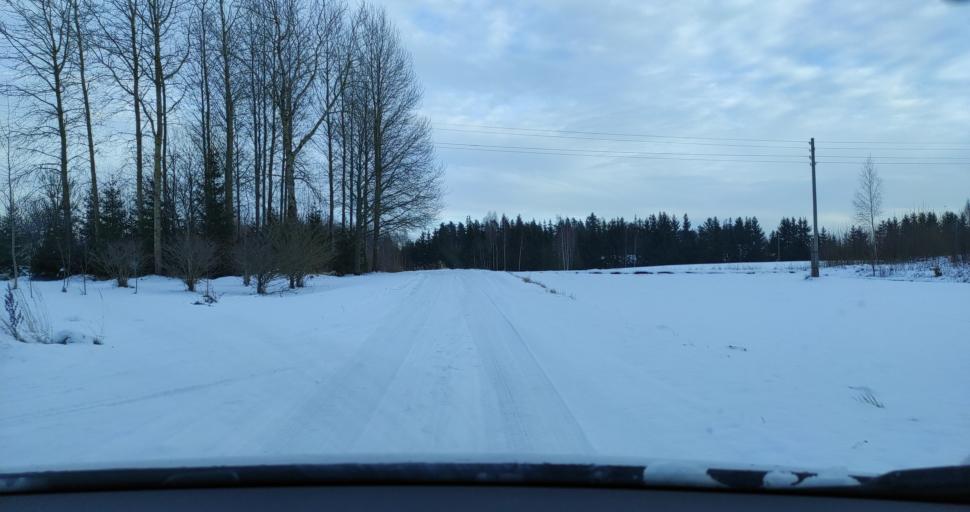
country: LV
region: Kuldigas Rajons
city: Kuldiga
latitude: 56.9425
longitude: 22.0418
